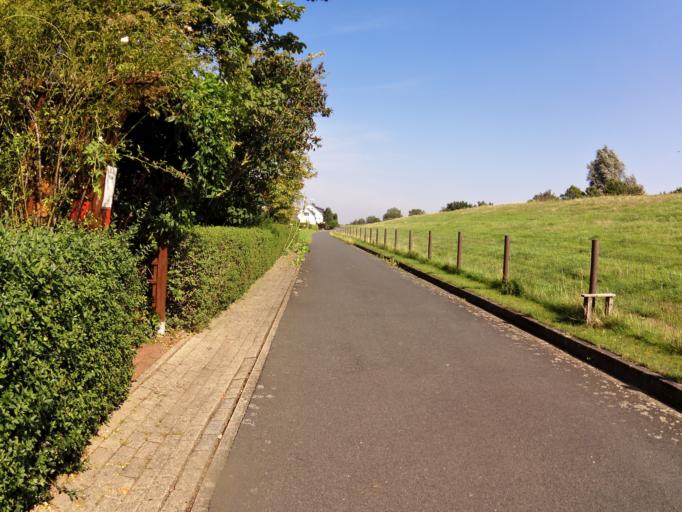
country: DE
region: Lower Saxony
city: Elsfleth
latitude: 53.2611
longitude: 8.4777
